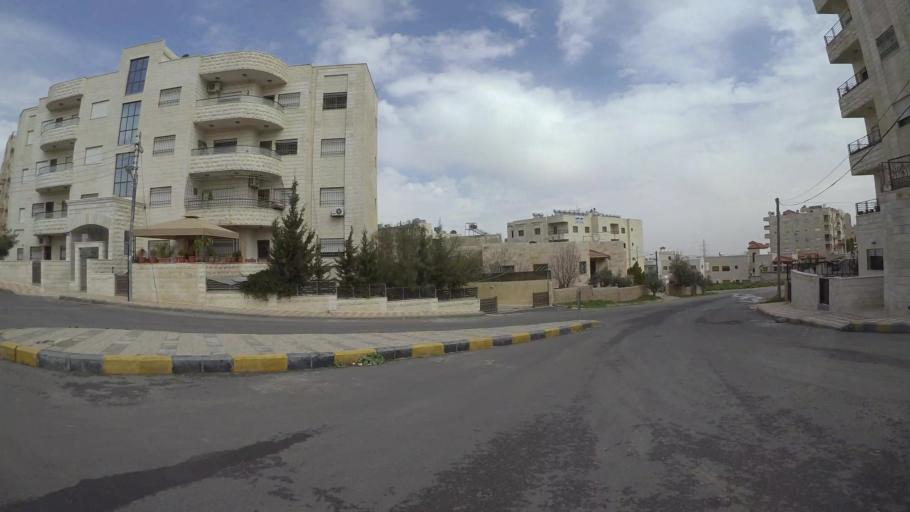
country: JO
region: Amman
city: Amman
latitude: 31.9960
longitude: 35.9341
